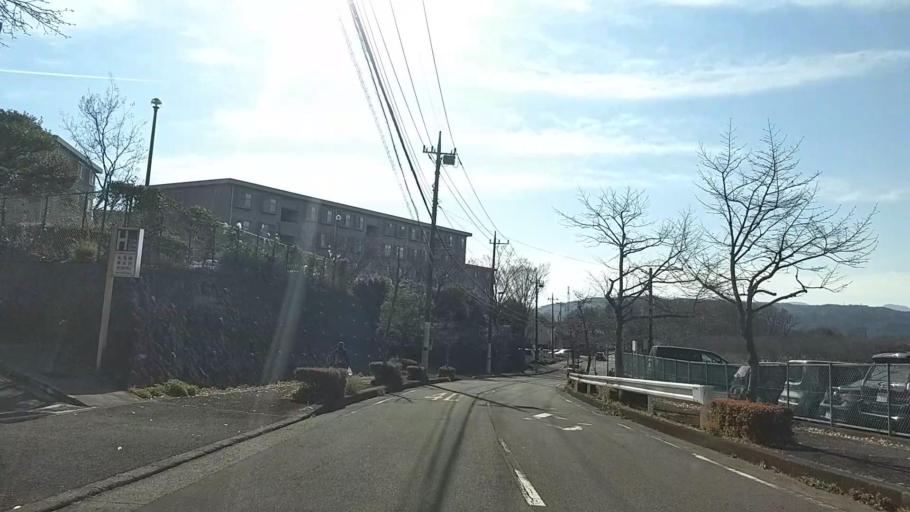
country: JP
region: Kanagawa
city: Hadano
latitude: 35.3555
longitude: 139.2238
